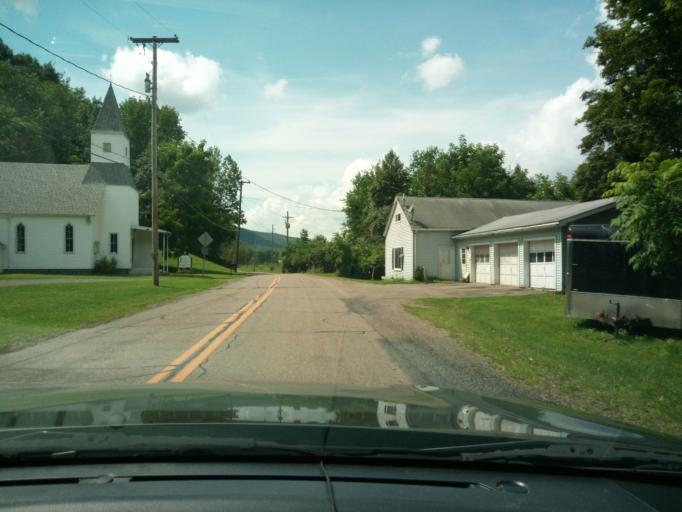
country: US
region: Pennsylvania
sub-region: Bradford County
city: South Waverly
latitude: 41.9879
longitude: -76.6180
